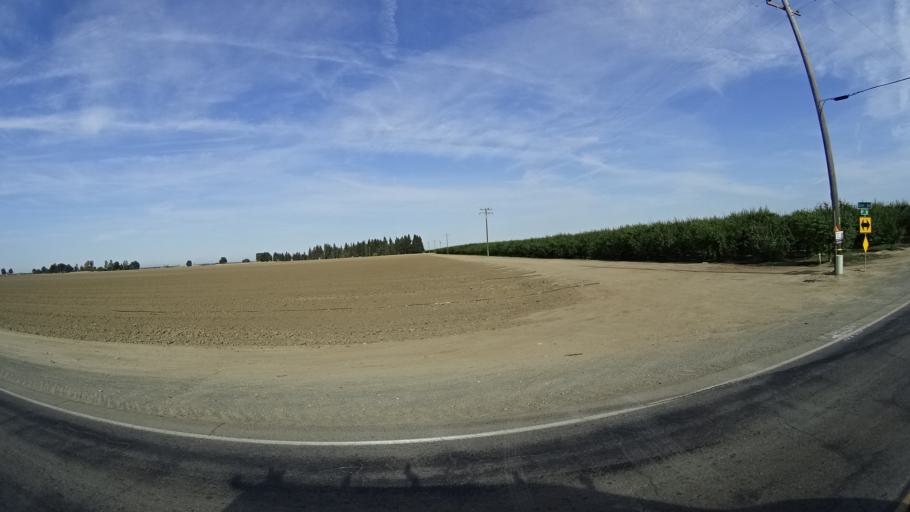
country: US
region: California
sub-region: Fresno County
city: Kingsburg
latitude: 36.4158
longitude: -119.5648
